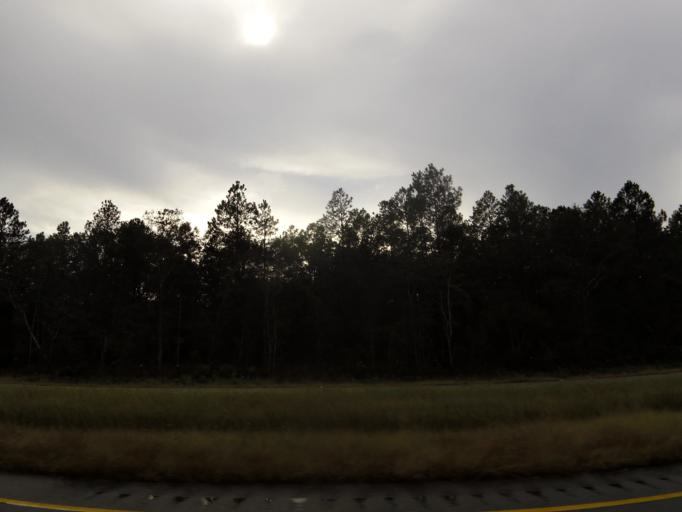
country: US
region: Georgia
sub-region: Wayne County
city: Jesup
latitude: 31.6121
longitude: -81.8599
